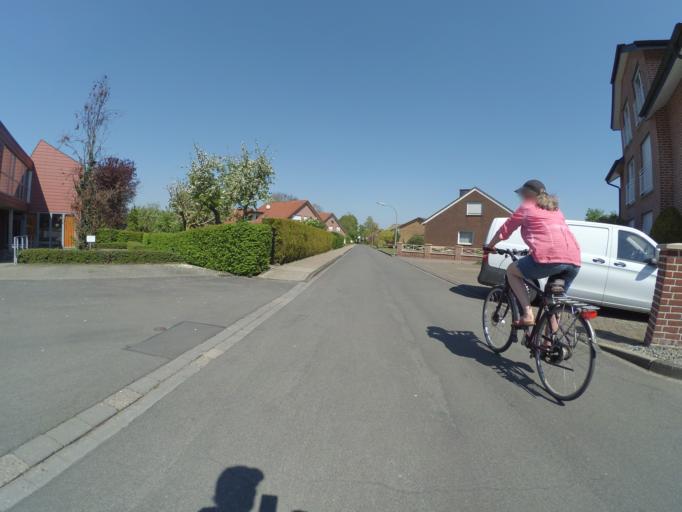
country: DE
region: North Rhine-Westphalia
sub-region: Regierungsbezirk Munster
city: Nordkirchen
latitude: 51.7395
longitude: 7.5271
